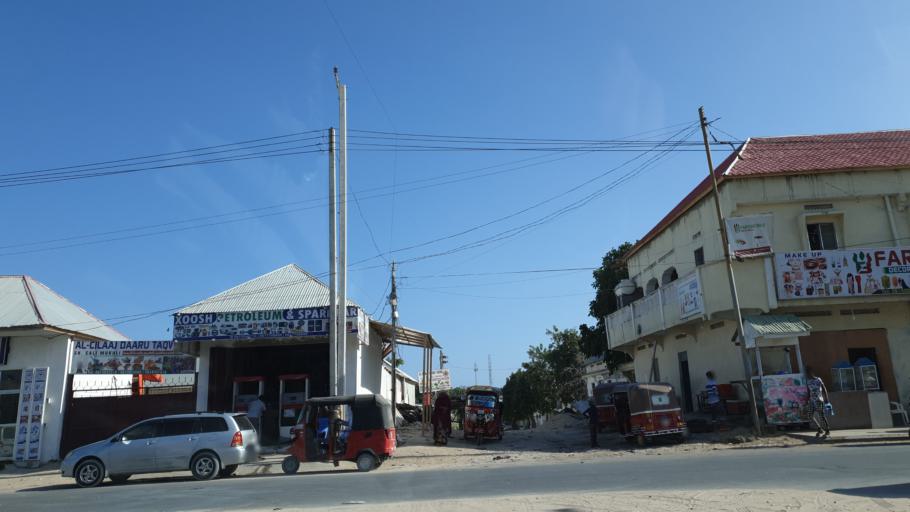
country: SO
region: Banaadir
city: Mogadishu
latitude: 2.0521
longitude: 45.3117
